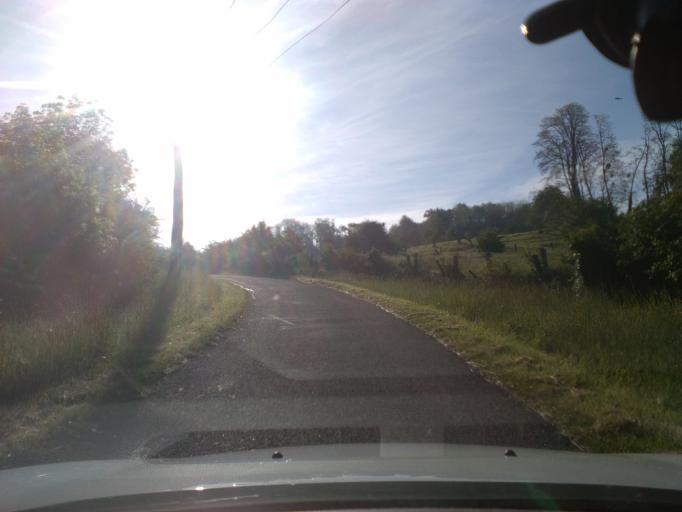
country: FR
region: Lorraine
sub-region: Departement des Vosges
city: Charmes
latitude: 48.3337
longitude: 6.2459
